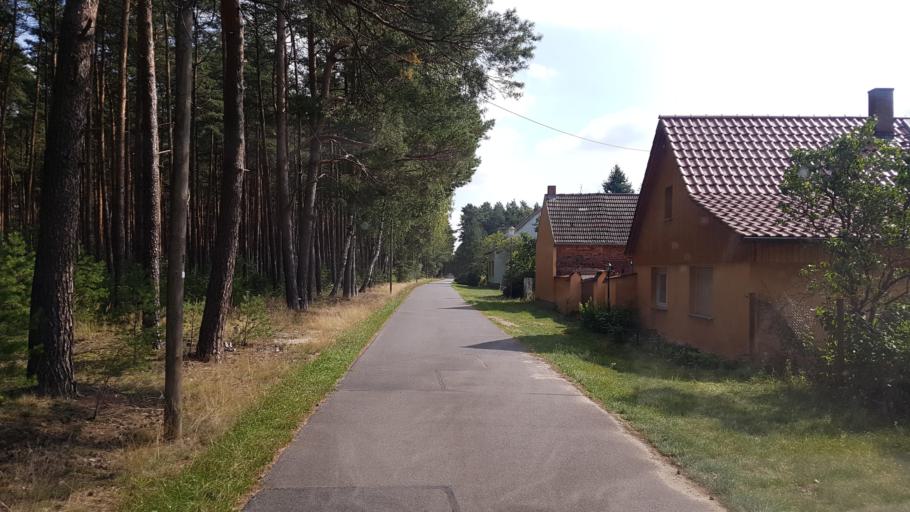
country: DE
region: Brandenburg
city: Hohenbucko
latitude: 51.7569
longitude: 13.5430
